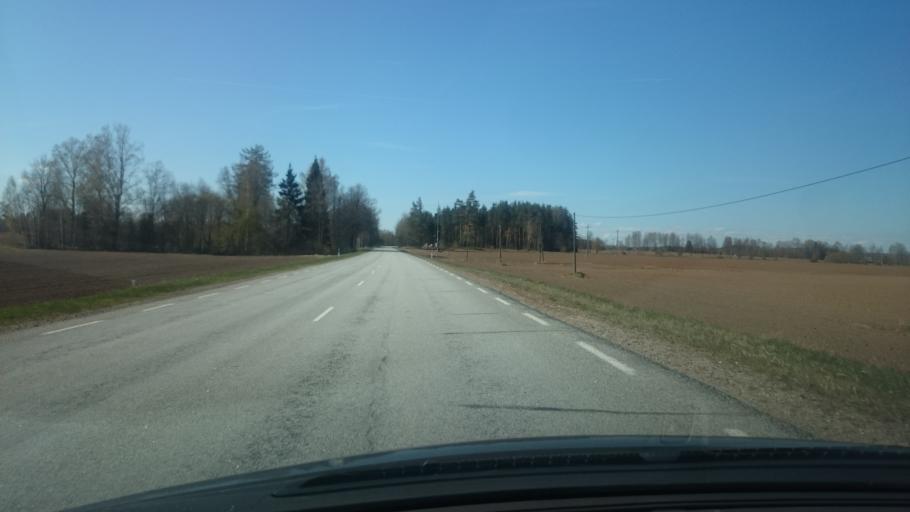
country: EE
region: Polvamaa
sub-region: Polva linn
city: Polva
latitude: 58.3098
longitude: 26.9967
